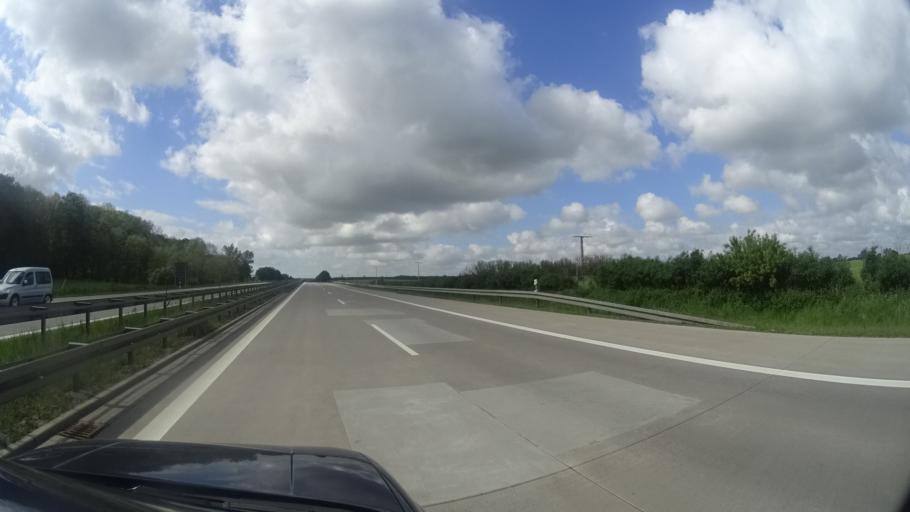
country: DE
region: Mecklenburg-Vorpommern
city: Laage
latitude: 53.9006
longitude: 12.2500
